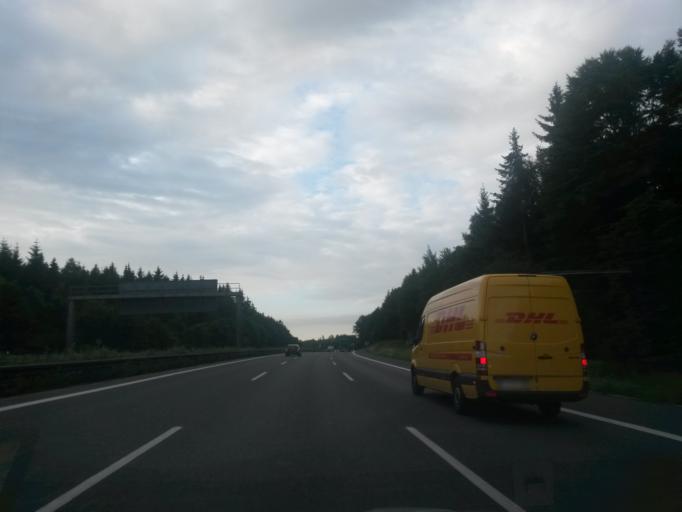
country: DE
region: Bavaria
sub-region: Upper Bavaria
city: Denkendorf
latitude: 48.9574
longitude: 11.4261
